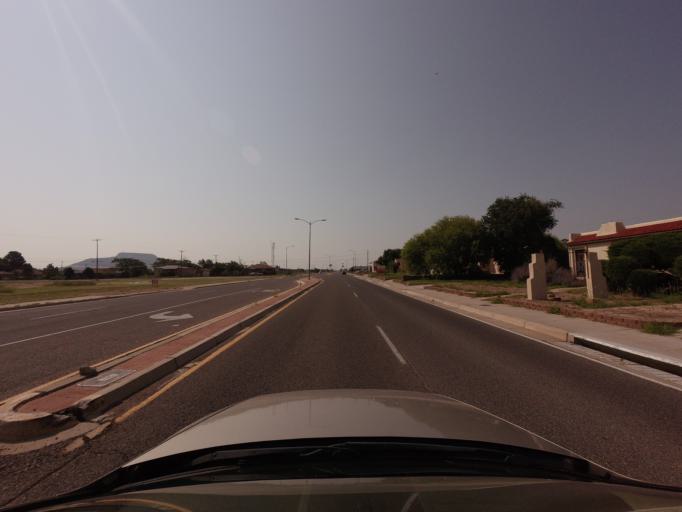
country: US
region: New Mexico
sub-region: Quay County
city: Tucumcari
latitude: 35.1627
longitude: -103.7250
